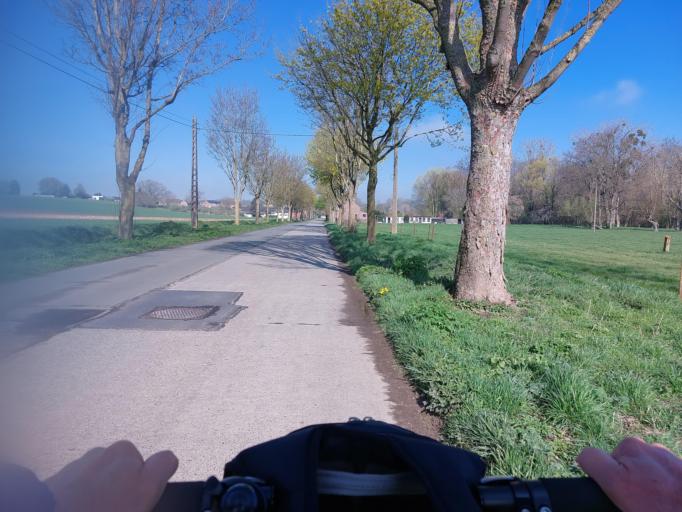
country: BE
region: Wallonia
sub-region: Province du Hainaut
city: Chasse Royale
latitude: 50.4068
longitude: 3.9737
